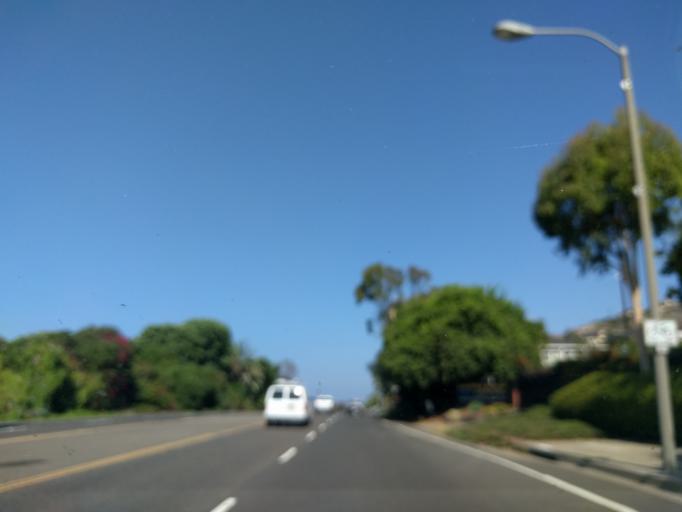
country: US
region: California
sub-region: Orange County
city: Laguna Niguel
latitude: 33.4911
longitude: -117.7321
